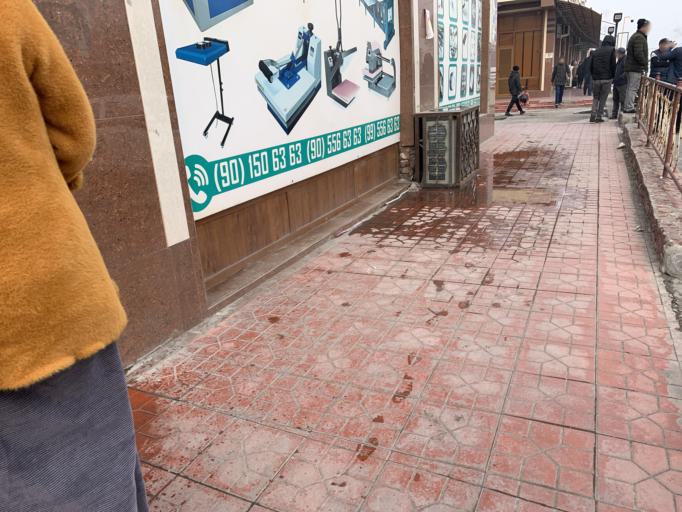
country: UZ
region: Fergana
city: Qo`qon
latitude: 40.5493
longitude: 70.9590
